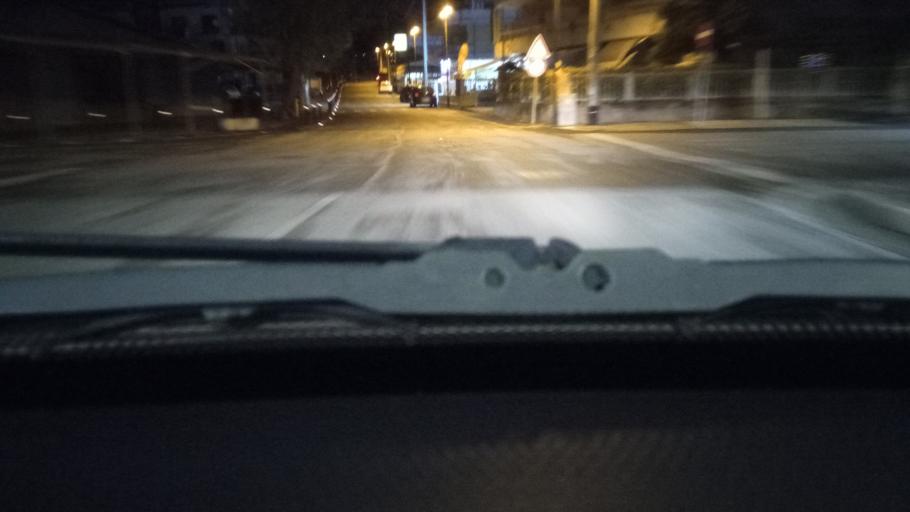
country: IT
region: Latium
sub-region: Provincia di Latina
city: Minturno
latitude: 41.2411
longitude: 13.7350
